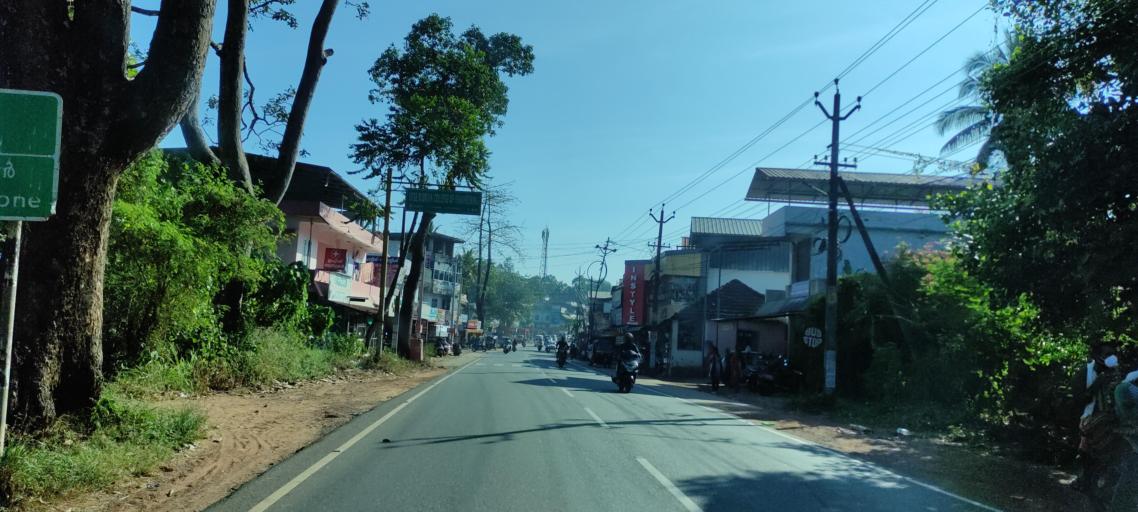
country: IN
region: Kerala
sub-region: Alappuzha
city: Kattanam
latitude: 9.1758
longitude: 76.6346
